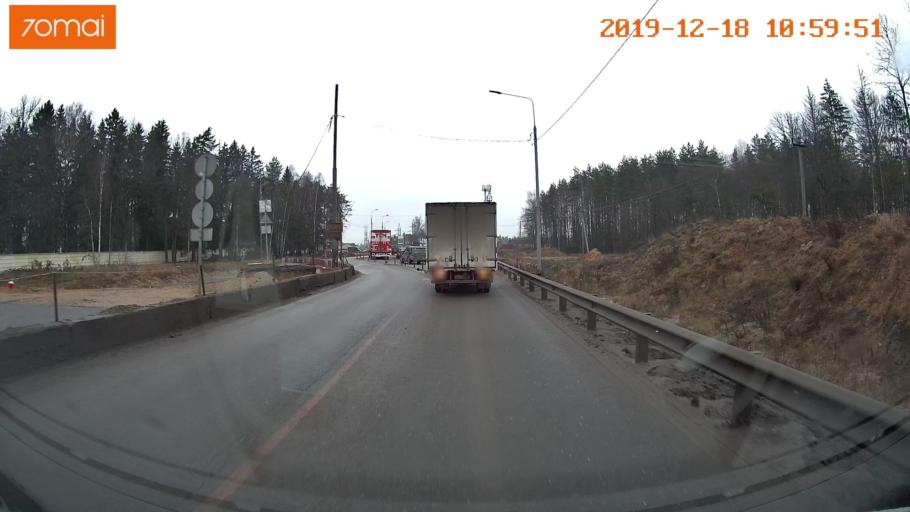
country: RU
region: Moskovskaya
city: Golitsyno
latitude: 55.5634
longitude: 36.9950
